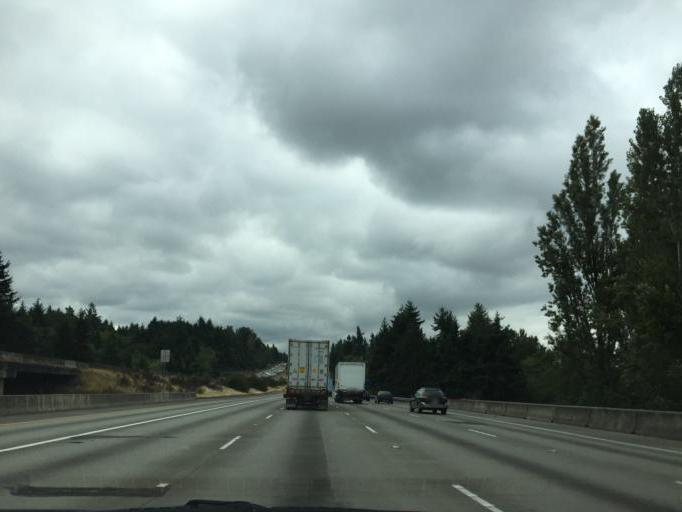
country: US
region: Washington
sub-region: King County
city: Lakeland North
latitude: 47.3701
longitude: -122.2937
